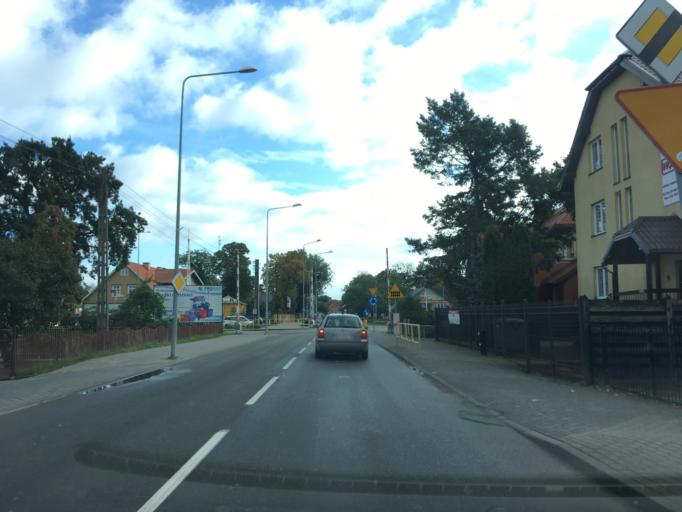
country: PL
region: Pomeranian Voivodeship
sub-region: Powiat nowodworski
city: Stegna
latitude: 54.3265
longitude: 19.1110
